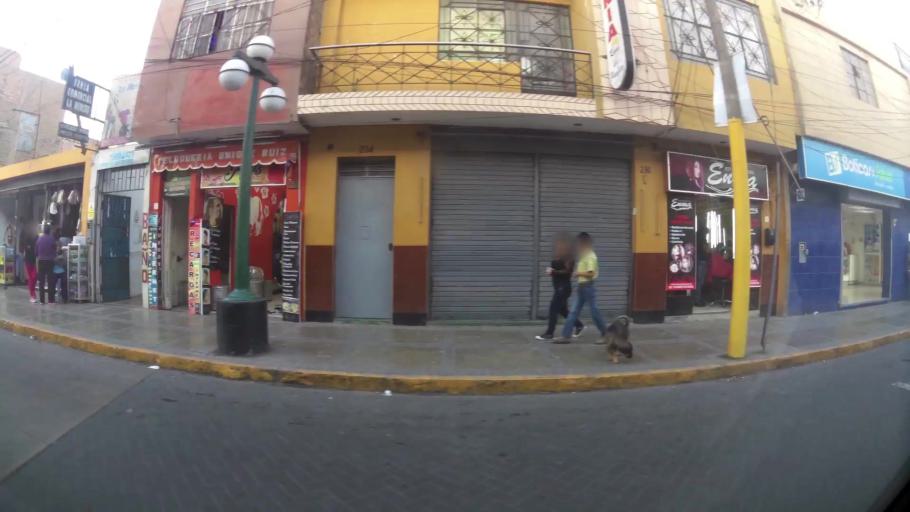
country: PE
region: Lima
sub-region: Huaura
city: Huacho
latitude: -11.1061
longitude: -77.6090
